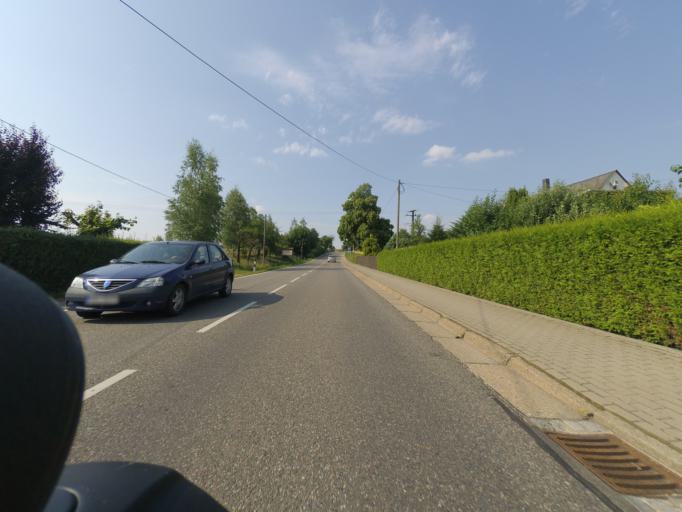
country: DE
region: Saxony
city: Geringswalde
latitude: 51.0858
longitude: 12.9218
